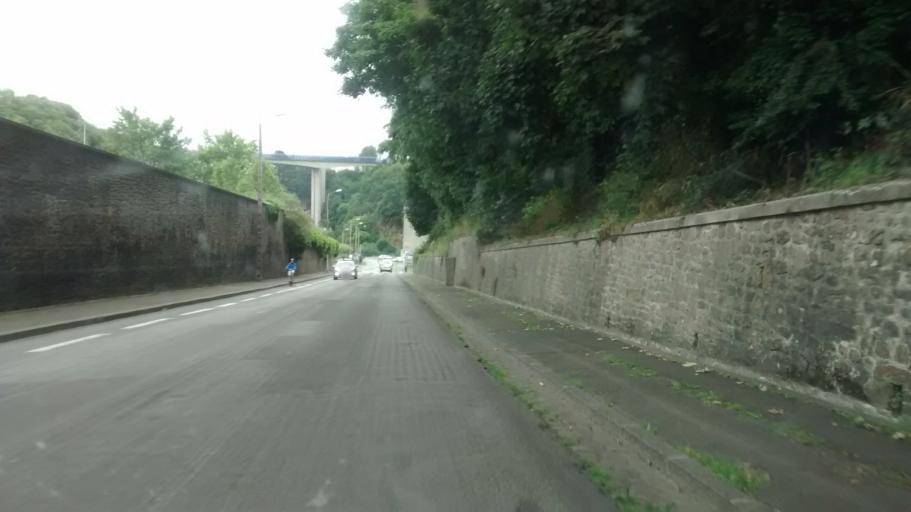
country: FR
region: Brittany
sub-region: Departement du Finistere
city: Brest
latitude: 48.3945
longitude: -4.4954
